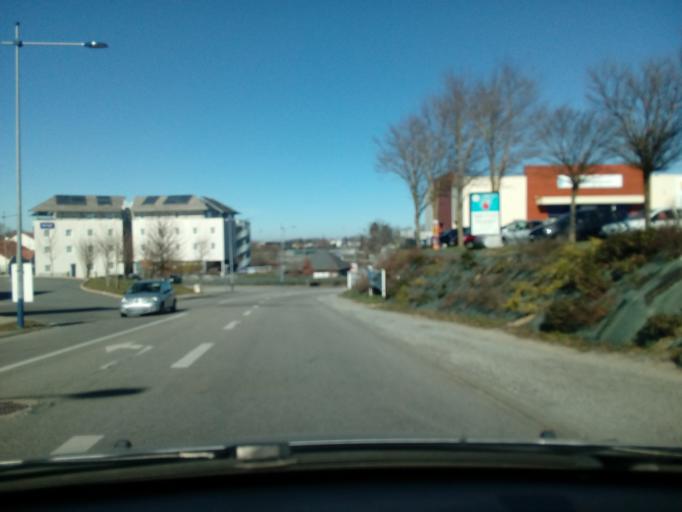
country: FR
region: Limousin
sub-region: Departement de la Creuse
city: Gueret
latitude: 46.1799
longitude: 1.8772
